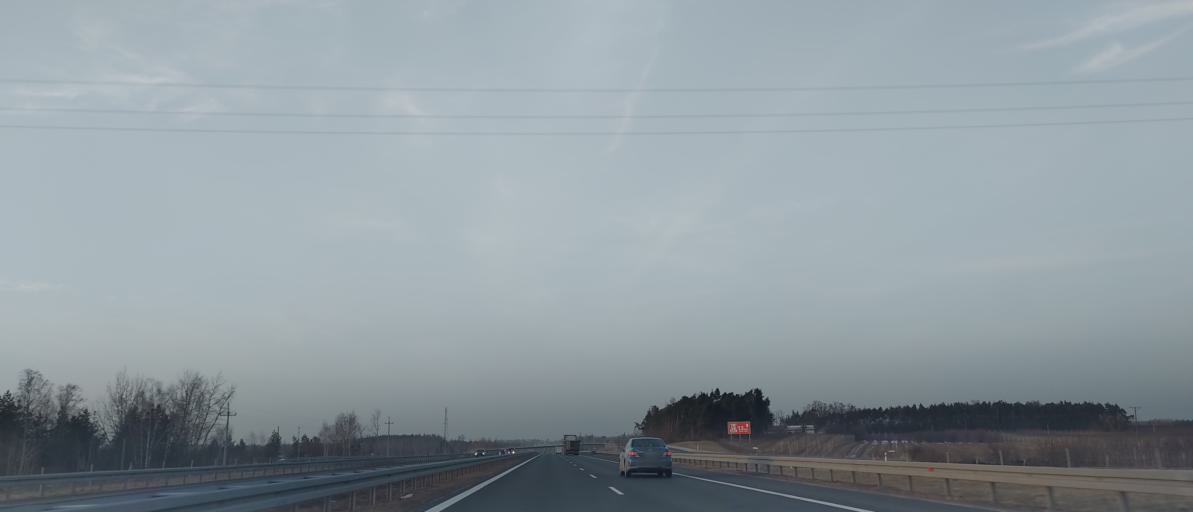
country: PL
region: Masovian Voivodeship
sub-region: Powiat bialobrzeski
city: Promna
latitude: 51.7176
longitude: 20.9220
